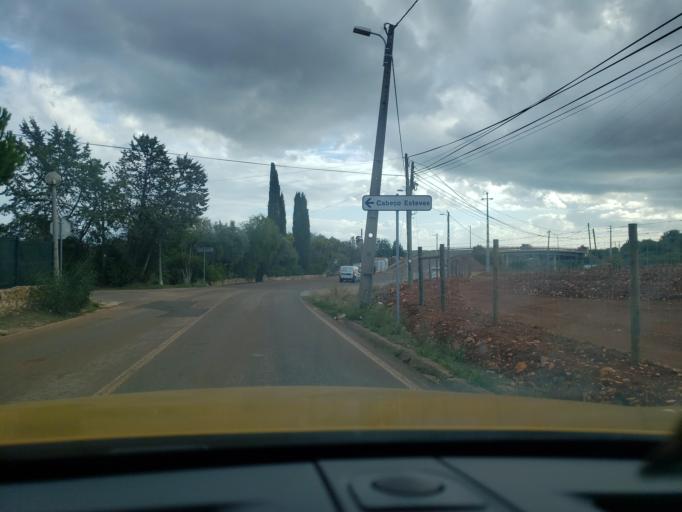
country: PT
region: Faro
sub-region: Portimao
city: Alvor
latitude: 37.1827
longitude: -8.5844
